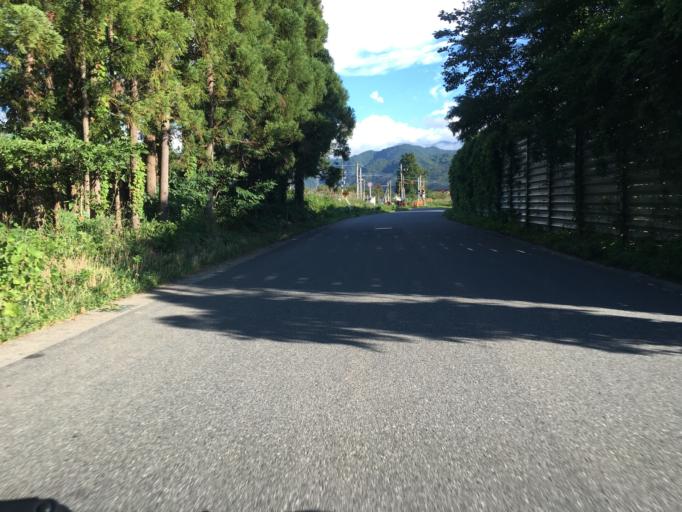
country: JP
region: Yamagata
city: Yonezawa
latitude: 37.8751
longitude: 140.1393
